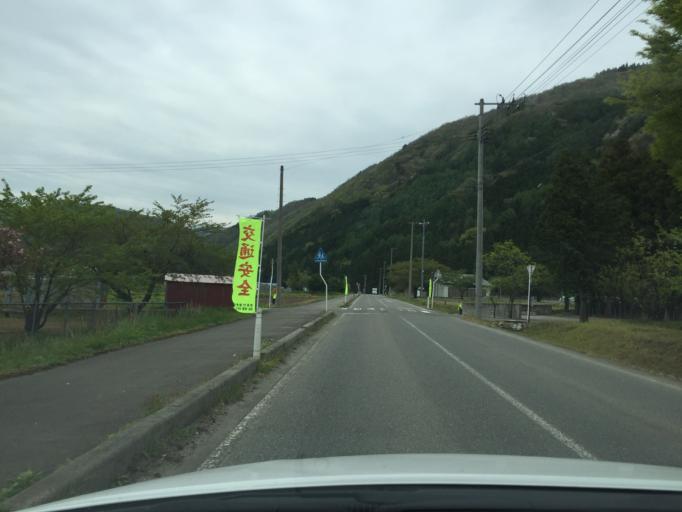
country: JP
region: Fukushima
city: Inawashiro
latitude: 37.5933
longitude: 140.1400
